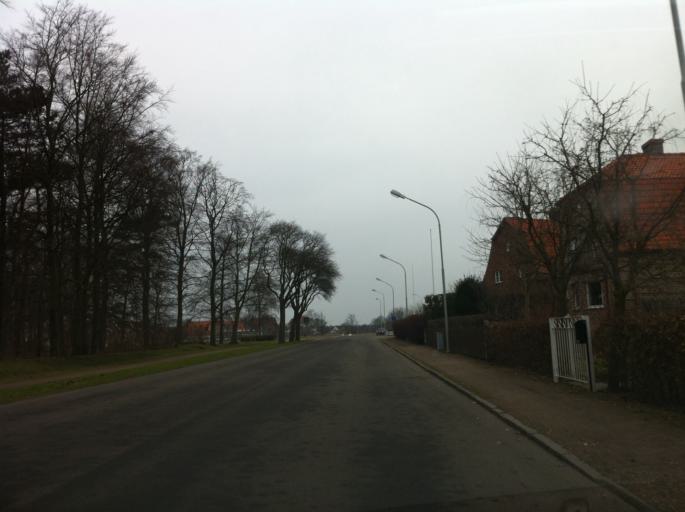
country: SE
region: Skane
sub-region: Landskrona
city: Landskrona
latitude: 55.8780
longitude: 12.8214
